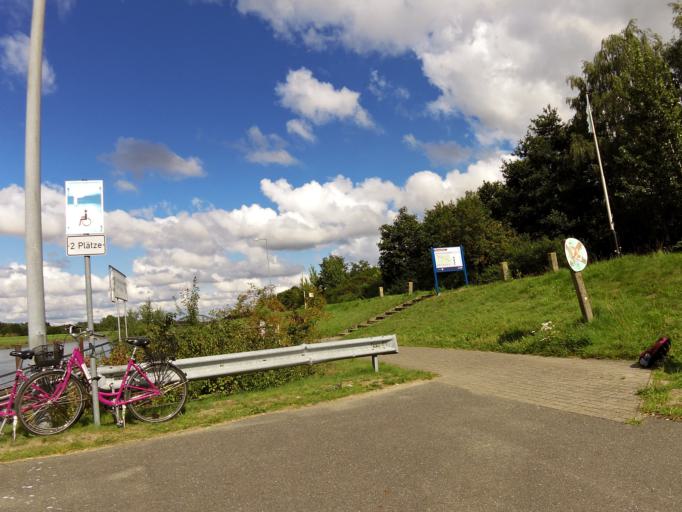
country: DE
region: Lower Saxony
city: Scharnebeck
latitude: 53.2982
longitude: 10.4903
